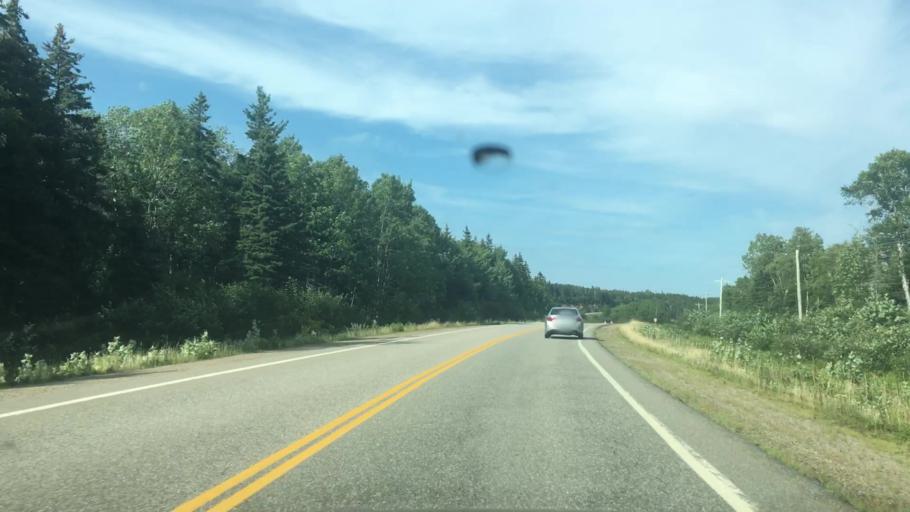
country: CA
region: Nova Scotia
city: Sydney Mines
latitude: 46.7167
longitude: -60.3523
